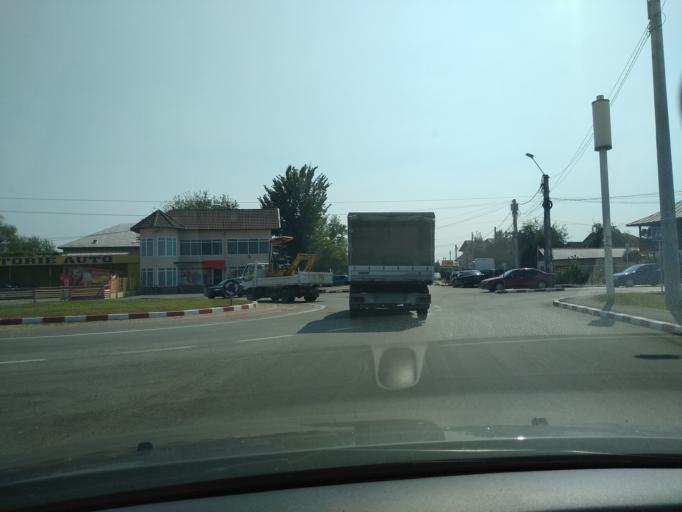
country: RO
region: Gorj
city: Targu Jiu
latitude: 45.0170
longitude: 23.2673
